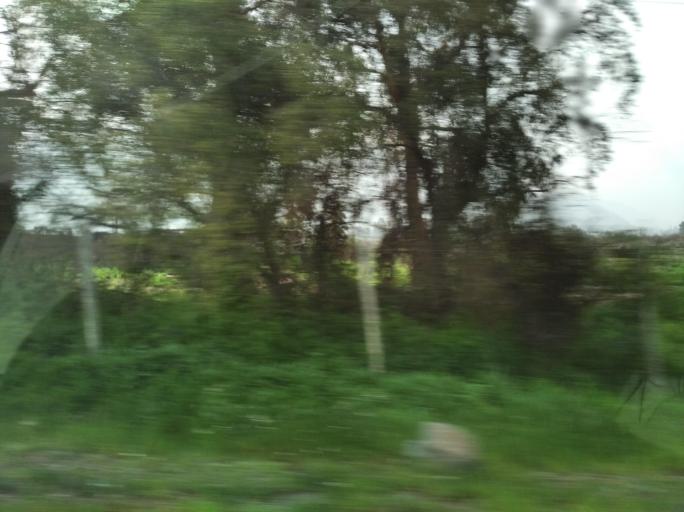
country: CL
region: Santiago Metropolitan
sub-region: Provincia de Chacabuco
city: Lampa
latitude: -33.2322
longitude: -70.9251
